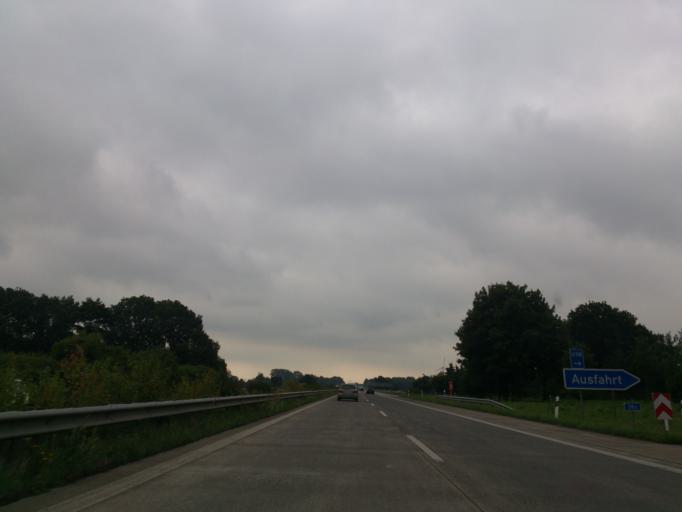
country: DE
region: Schleswig-Holstein
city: Neuenbrook
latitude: 53.8713
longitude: 9.5604
